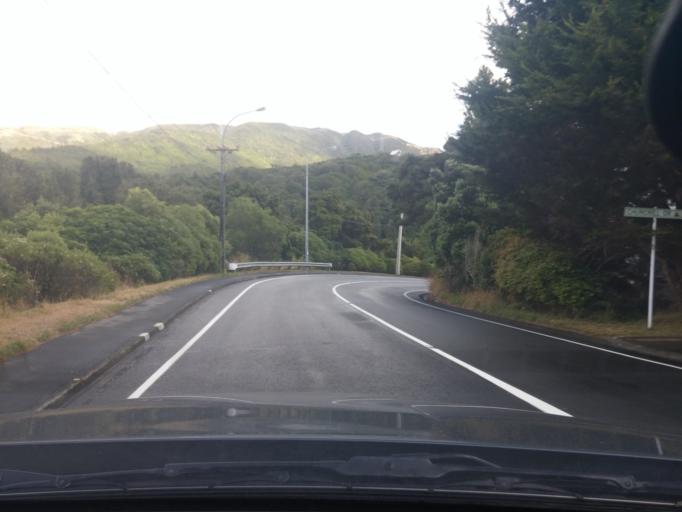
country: NZ
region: Wellington
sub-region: Wellington City
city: Kelburn
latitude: -41.2670
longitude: 174.7618
